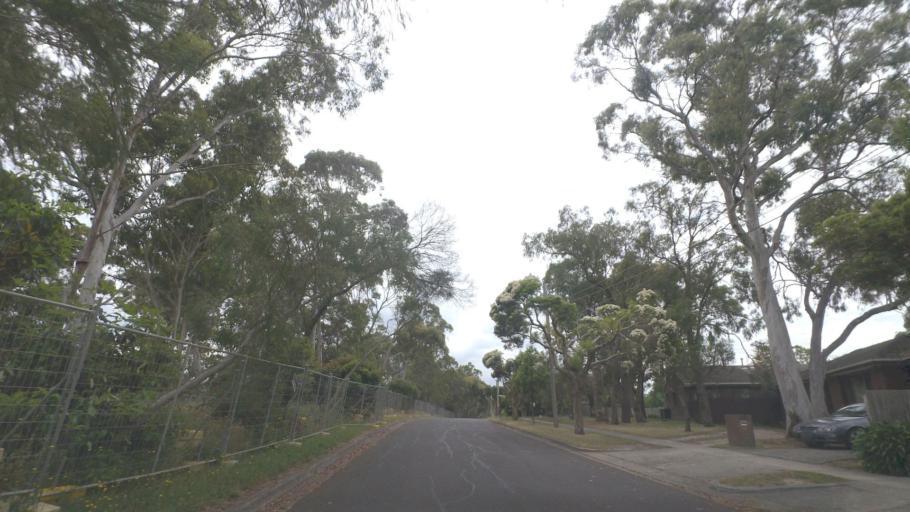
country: AU
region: Victoria
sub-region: Maroondah
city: Croydon North
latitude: -37.7835
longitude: 145.3035
